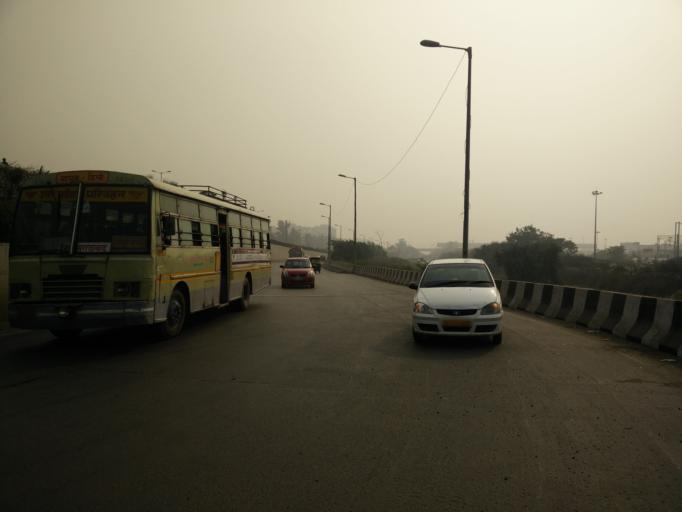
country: IN
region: Uttar Pradesh
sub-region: Gautam Buddha Nagar
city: Noida
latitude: 28.6528
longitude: 77.3193
